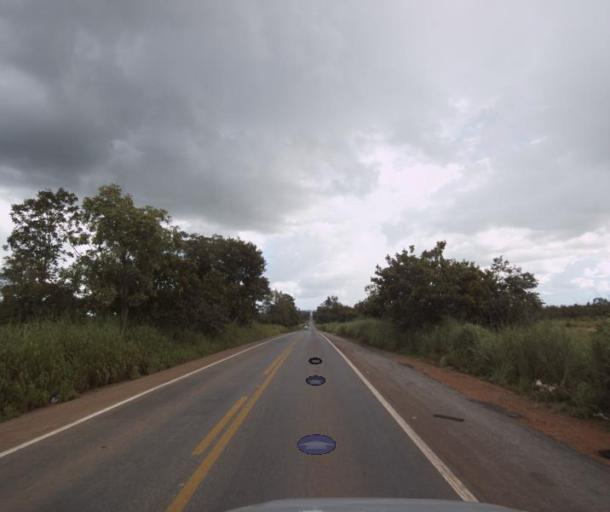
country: BR
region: Goias
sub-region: Porangatu
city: Porangatu
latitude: -13.3261
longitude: -49.1194
